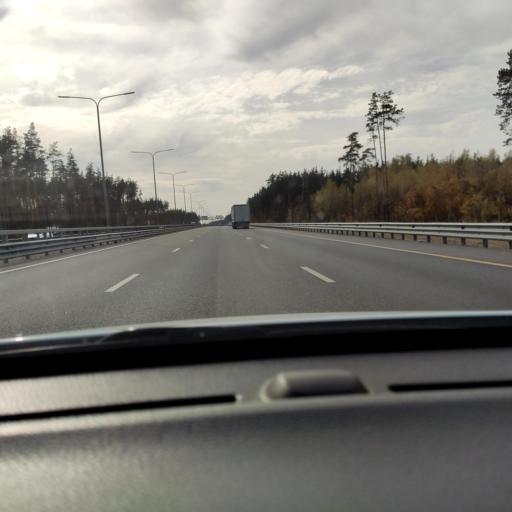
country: RU
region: Voronezj
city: Somovo
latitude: 51.7059
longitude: 39.3058
